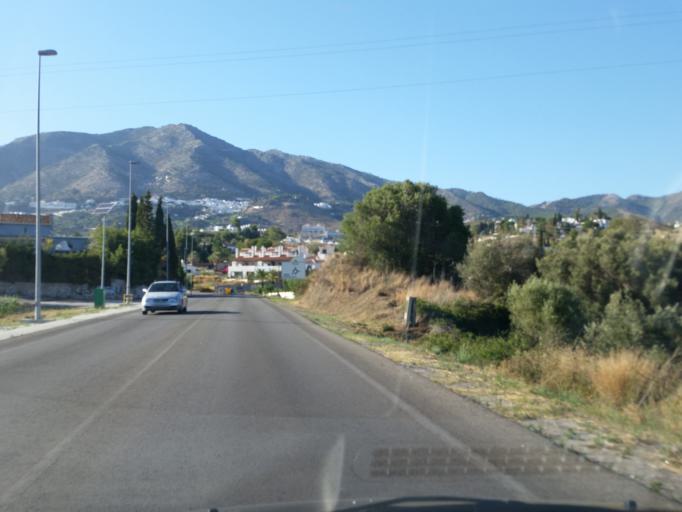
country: ES
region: Andalusia
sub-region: Provincia de Malaga
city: Mijas
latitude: 36.5727
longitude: -4.6350
